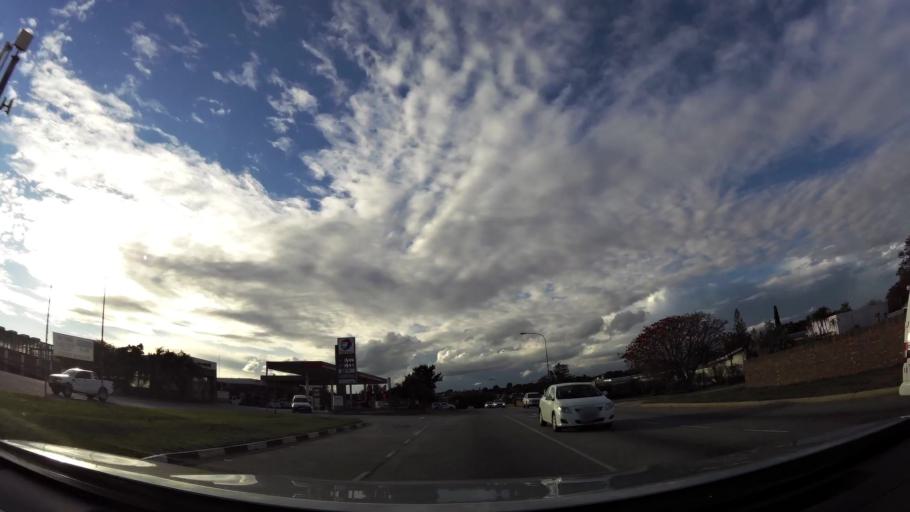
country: ZA
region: Eastern Cape
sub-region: Nelson Mandela Bay Metropolitan Municipality
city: Port Elizabeth
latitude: -33.9566
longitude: 25.5046
